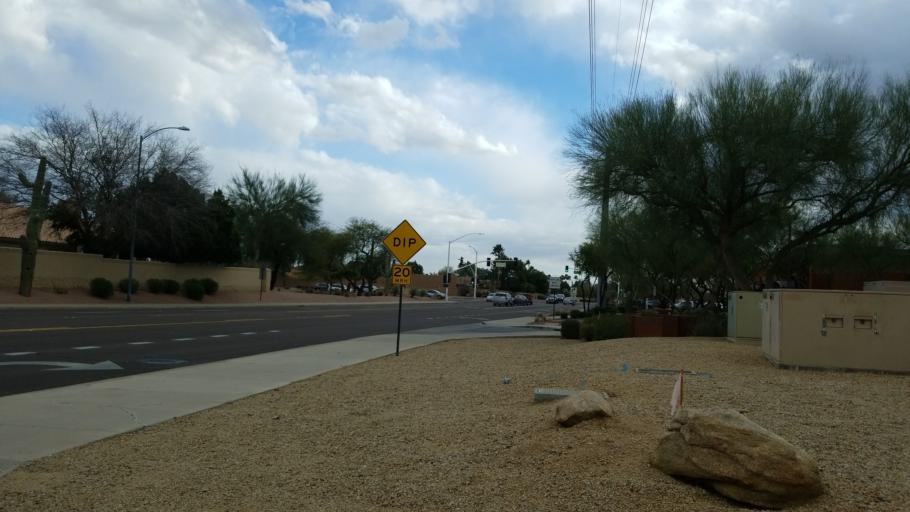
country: US
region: Arizona
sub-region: Maricopa County
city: Paradise Valley
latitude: 33.6199
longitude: -111.8872
